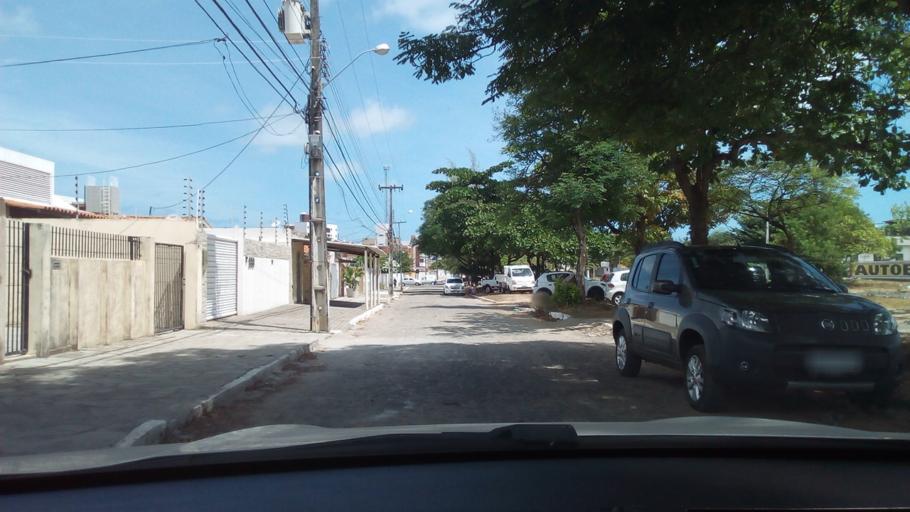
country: BR
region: Paraiba
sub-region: Joao Pessoa
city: Joao Pessoa
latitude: -7.1457
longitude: -34.8373
